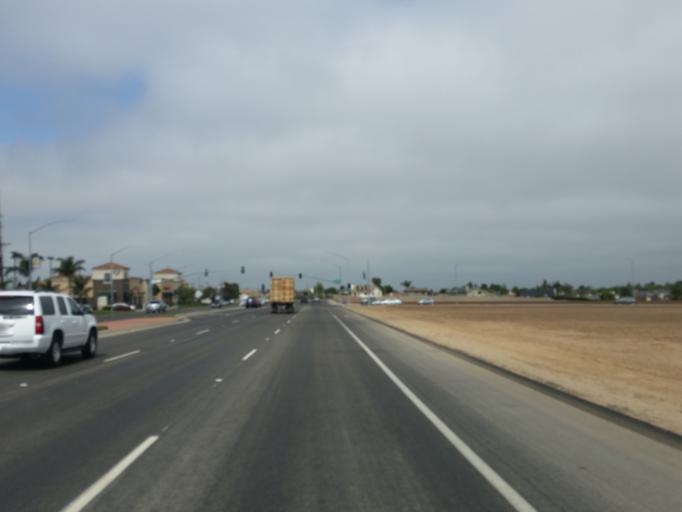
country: US
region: California
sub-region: Santa Barbara County
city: Santa Maria
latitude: 34.9236
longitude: -120.4239
